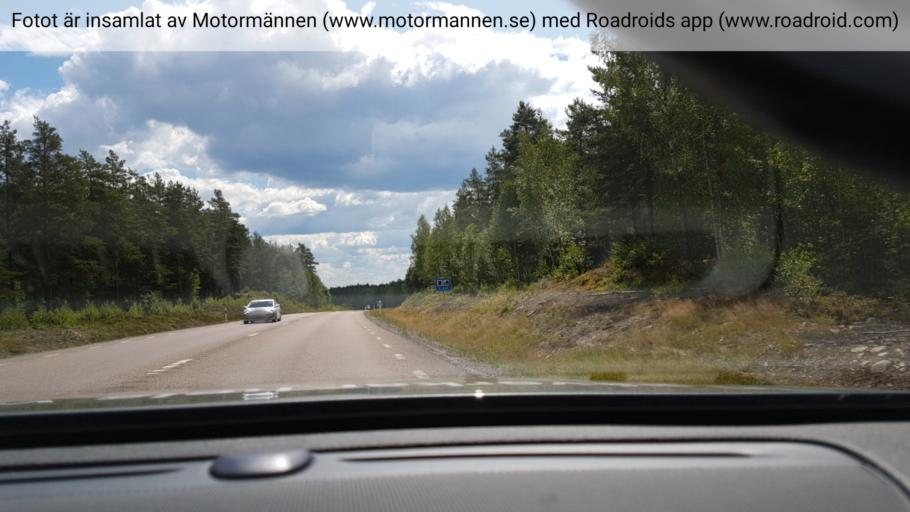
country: SE
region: Dalarna
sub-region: Faluns Kommun
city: Falun
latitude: 60.6360
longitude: 15.5889
